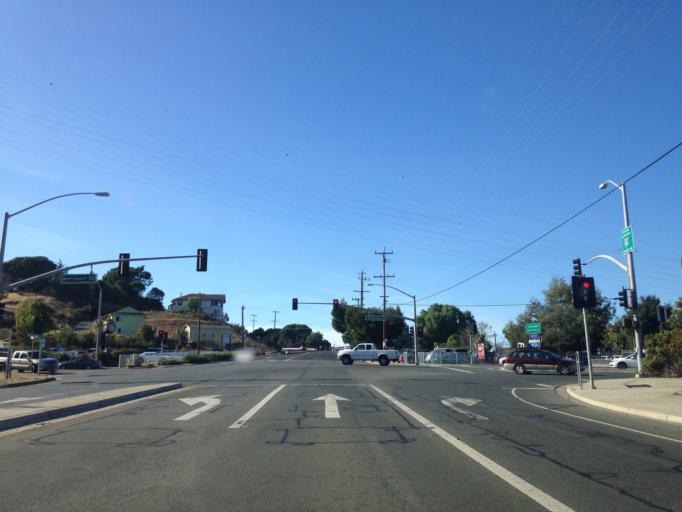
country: US
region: California
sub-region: Contra Costa County
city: Crockett
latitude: 38.0546
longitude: -122.2298
